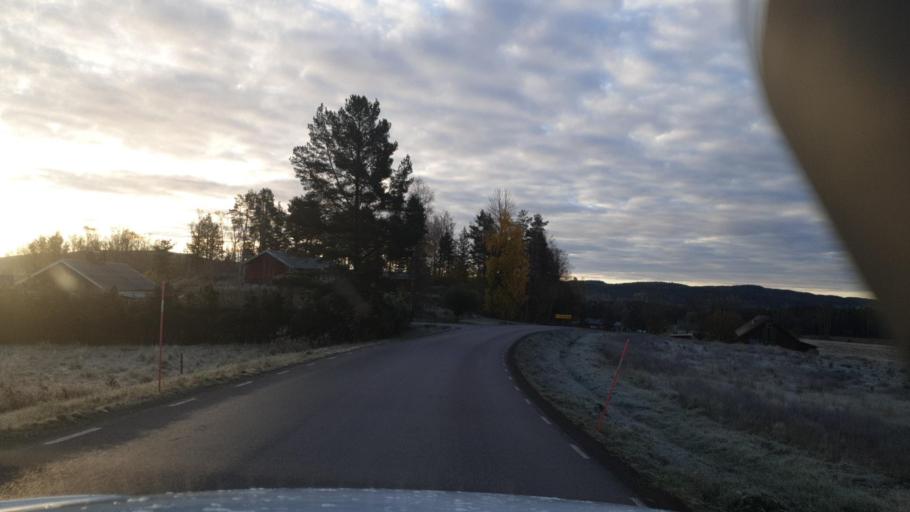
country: SE
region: Vaermland
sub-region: Eda Kommun
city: Charlottenberg
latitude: 59.7442
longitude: 12.1660
